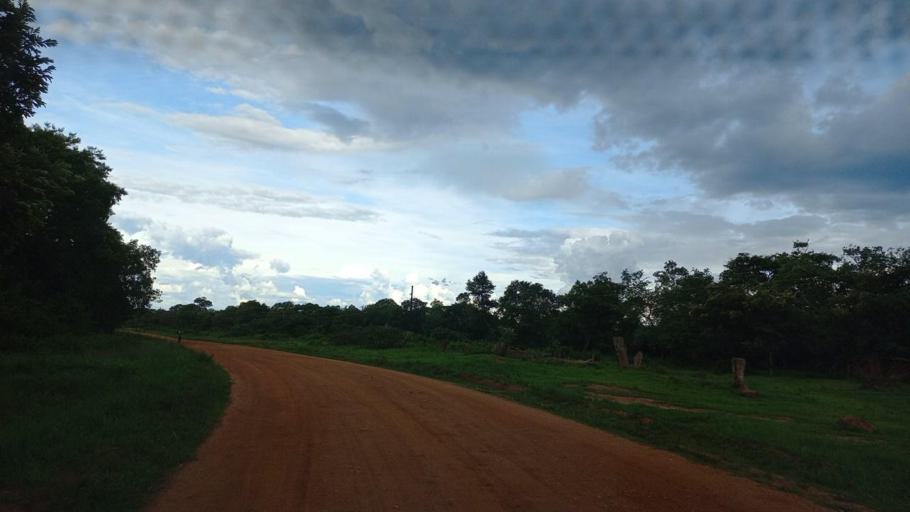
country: ZM
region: North-Western
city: Mwinilunga
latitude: -11.7742
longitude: 24.4043
